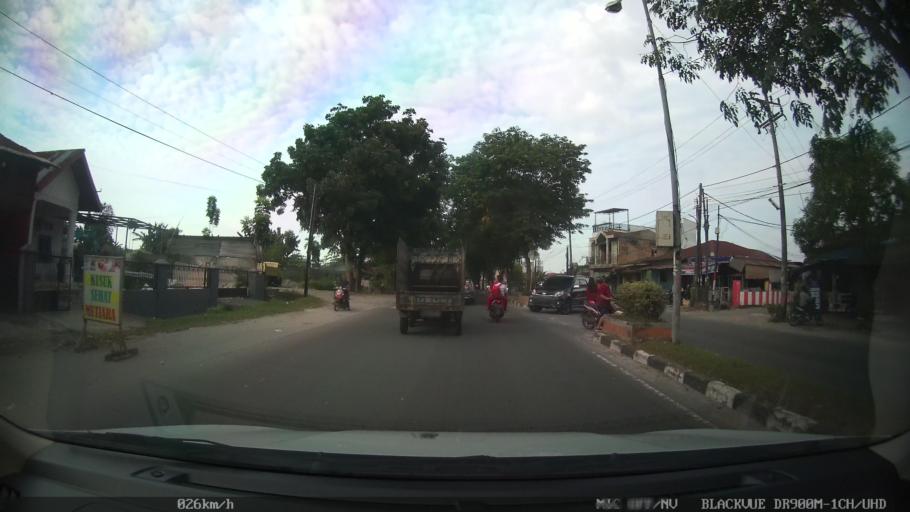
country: ID
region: North Sumatra
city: Sunggal
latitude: 3.5567
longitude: 98.6160
